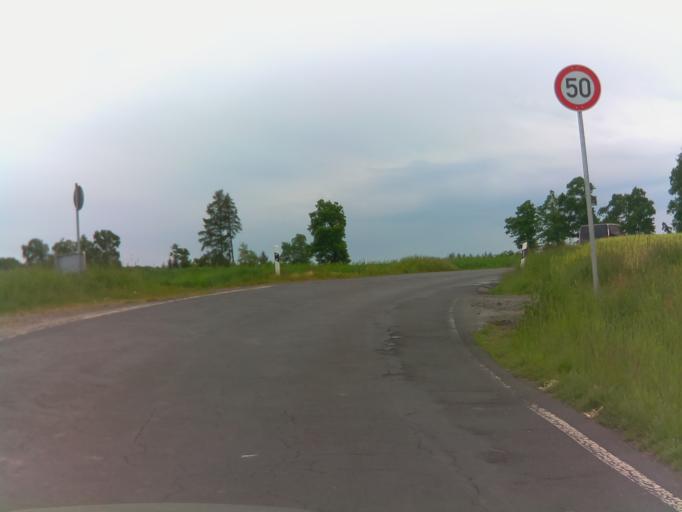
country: DE
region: Hesse
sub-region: Regierungsbezirk Kassel
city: Willingshausen
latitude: 50.8629
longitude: 9.1636
